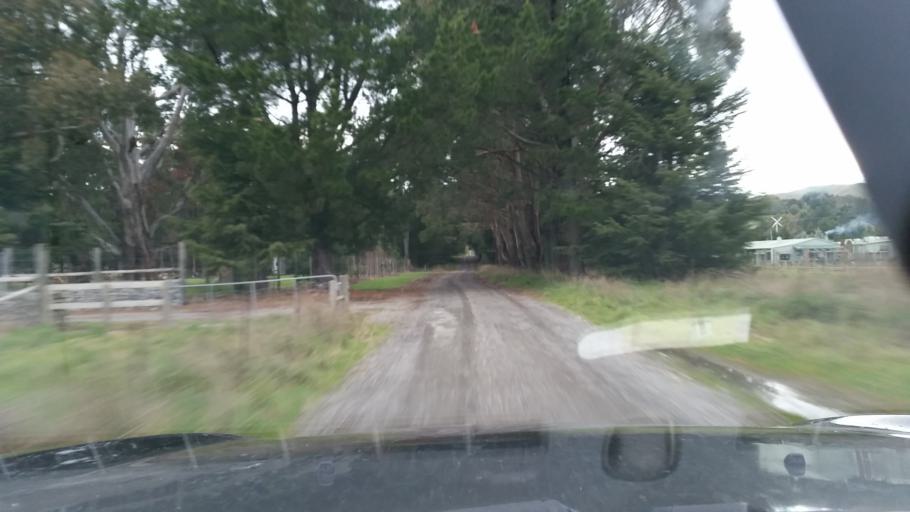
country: NZ
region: Marlborough
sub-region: Marlborough District
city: Blenheim
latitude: -41.5353
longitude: 173.6134
